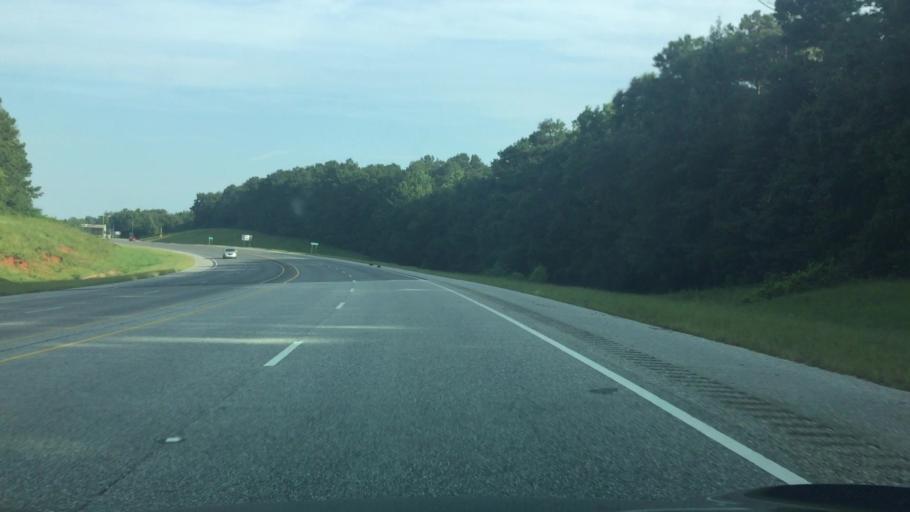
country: US
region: Alabama
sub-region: Butler County
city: Georgiana
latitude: 31.5137
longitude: -86.7025
